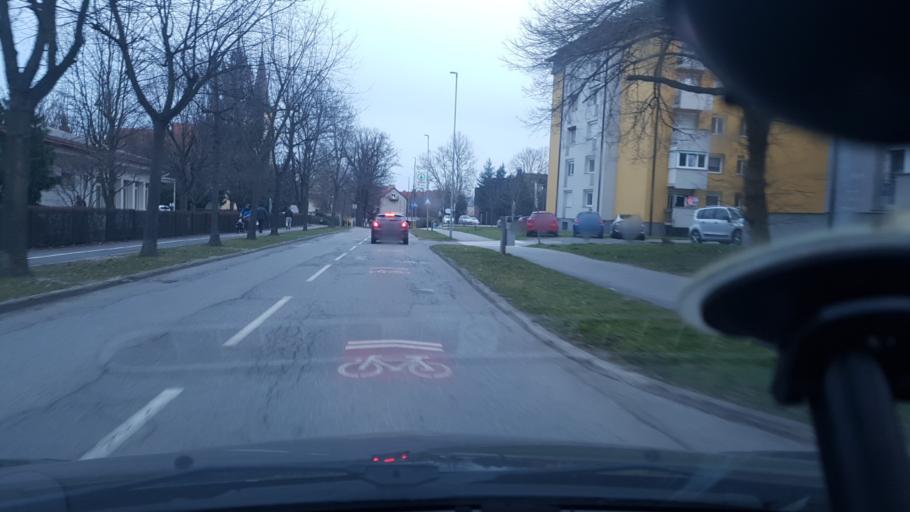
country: SI
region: Ptuj
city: Ptuj
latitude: 46.4245
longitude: 15.8732
